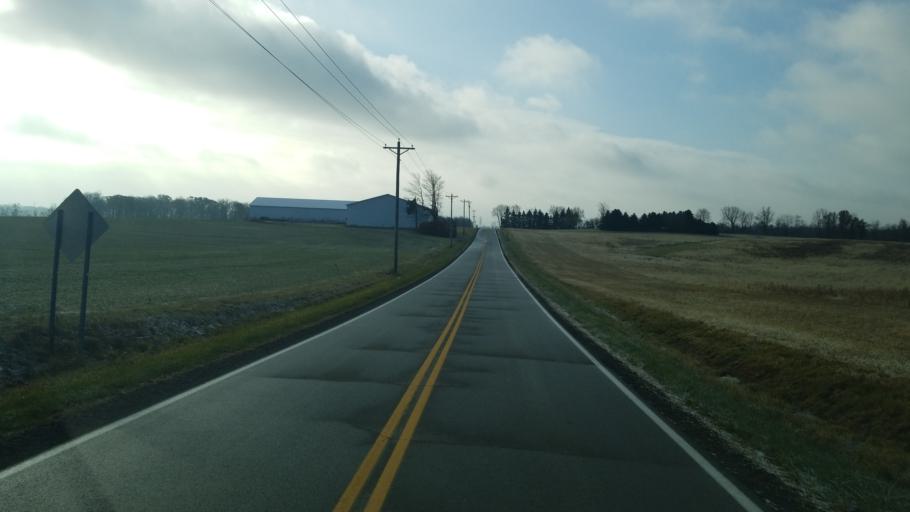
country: US
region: Ohio
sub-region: Richland County
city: Shelby
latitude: 40.8979
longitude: -82.7438
